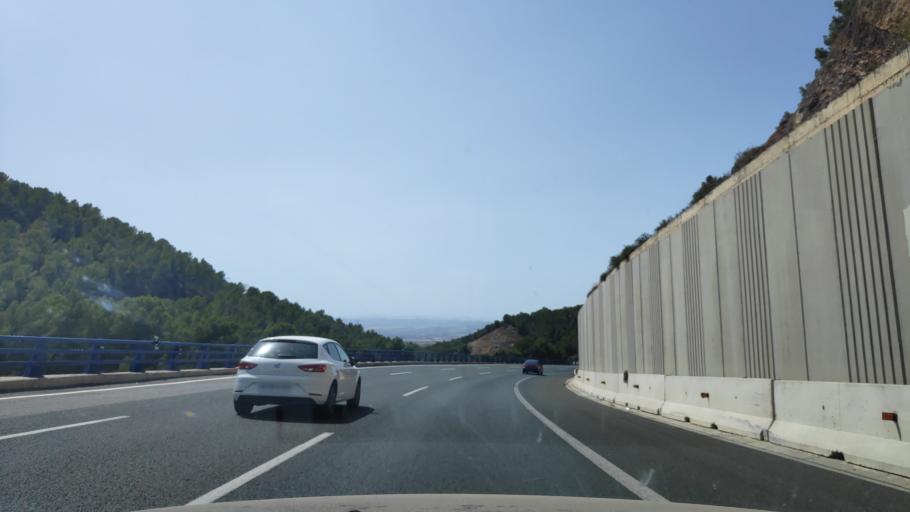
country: ES
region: Murcia
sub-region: Murcia
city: Murcia
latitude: 37.9057
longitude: -1.1482
